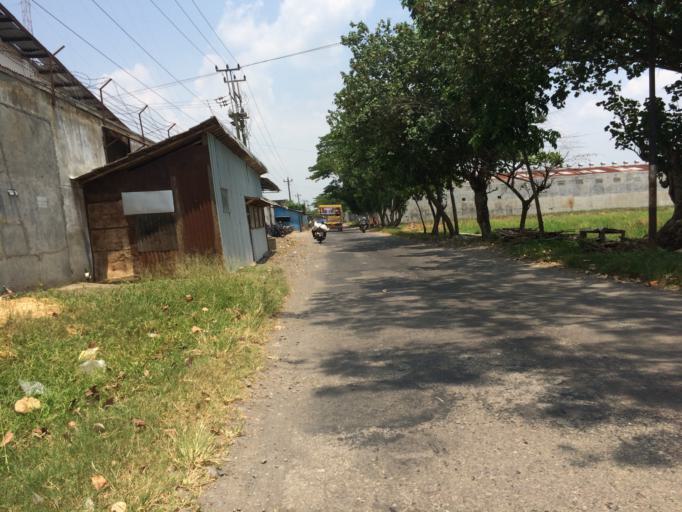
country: ID
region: Central Java
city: Grogol
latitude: -7.6161
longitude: 110.8240
